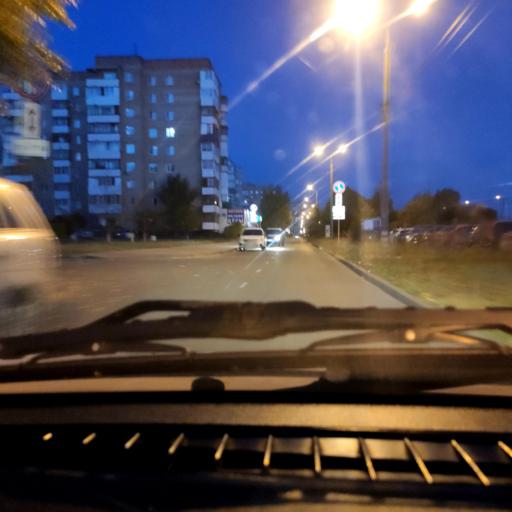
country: RU
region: Samara
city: Zhigulevsk
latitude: 53.4744
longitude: 49.5316
